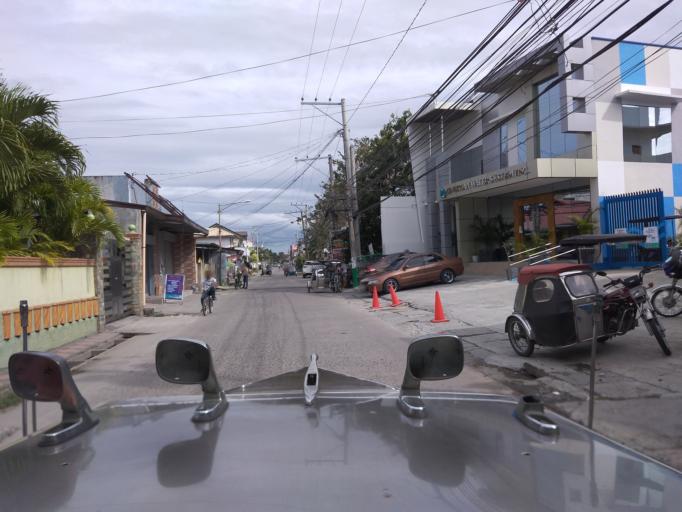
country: PH
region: Central Luzon
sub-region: Province of Pampanga
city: Mexico
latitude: 15.0640
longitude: 120.7237
